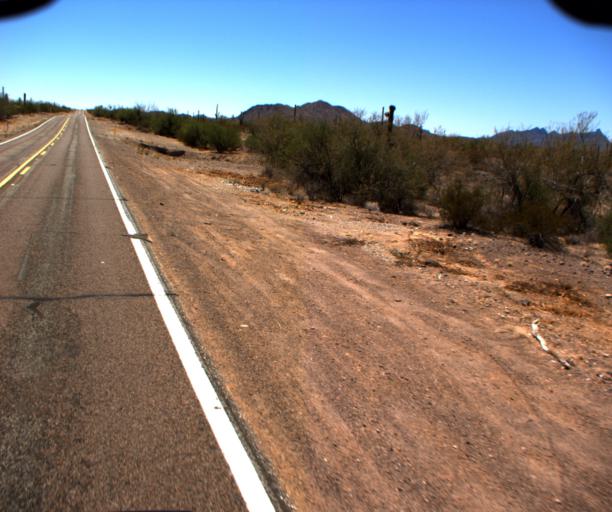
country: US
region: Arizona
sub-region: Pima County
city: Ajo
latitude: 32.2279
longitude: -112.7087
